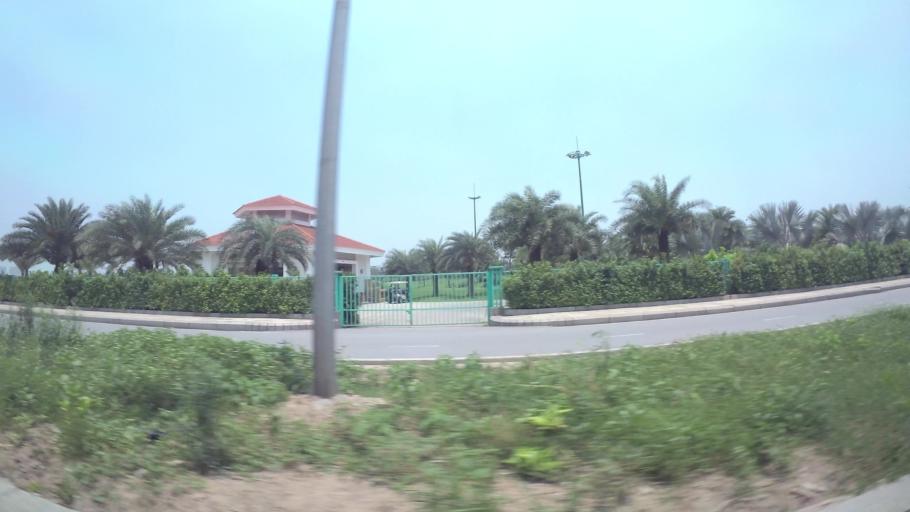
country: VN
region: Ha Noi
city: Trau Quy
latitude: 21.0383
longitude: 105.8961
